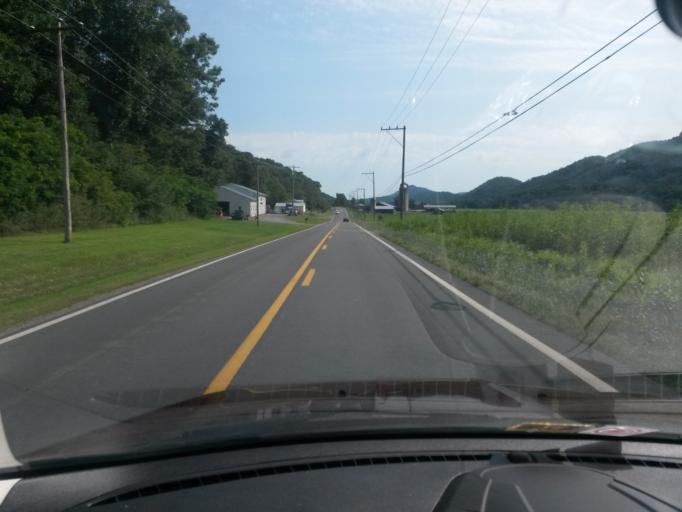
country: US
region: West Virginia
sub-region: Hardy County
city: Moorefield
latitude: 39.0146
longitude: -78.7659
